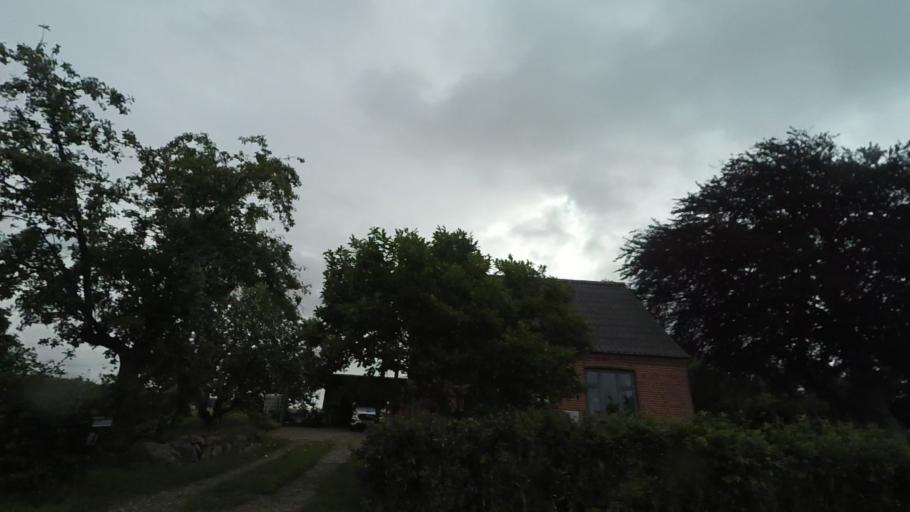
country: DK
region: Central Jutland
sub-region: Syddjurs Kommune
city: Ronde
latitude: 56.3138
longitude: 10.4619
